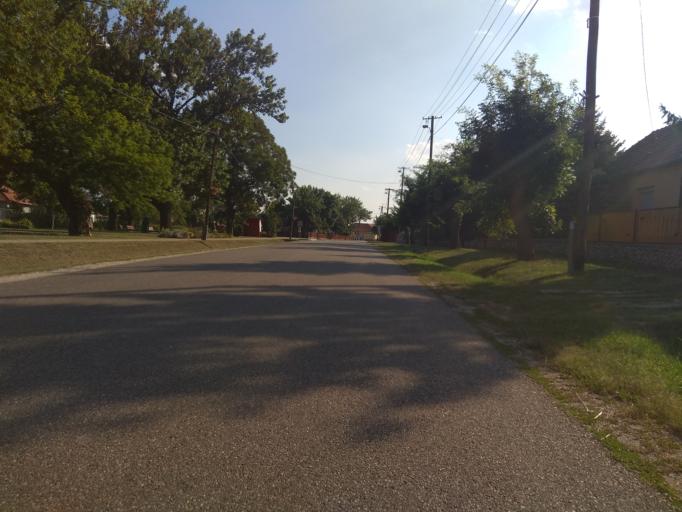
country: HU
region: Borsod-Abauj-Zemplen
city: Mezokeresztes
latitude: 47.8569
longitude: 20.6786
